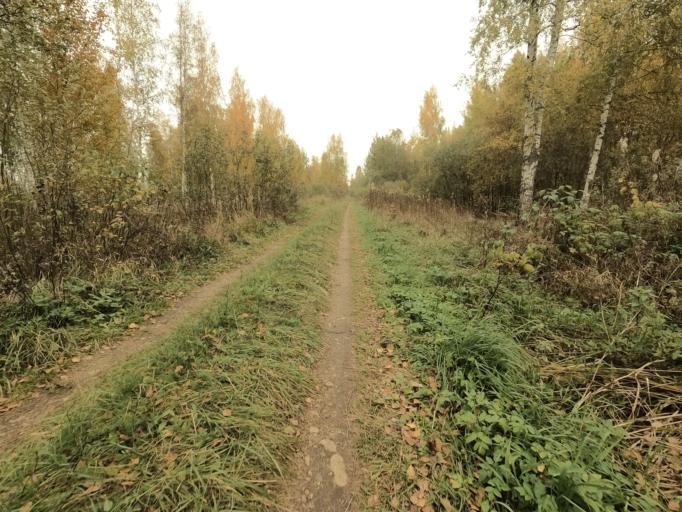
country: RU
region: Novgorod
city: Pankovka
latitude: 58.8738
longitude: 30.9387
